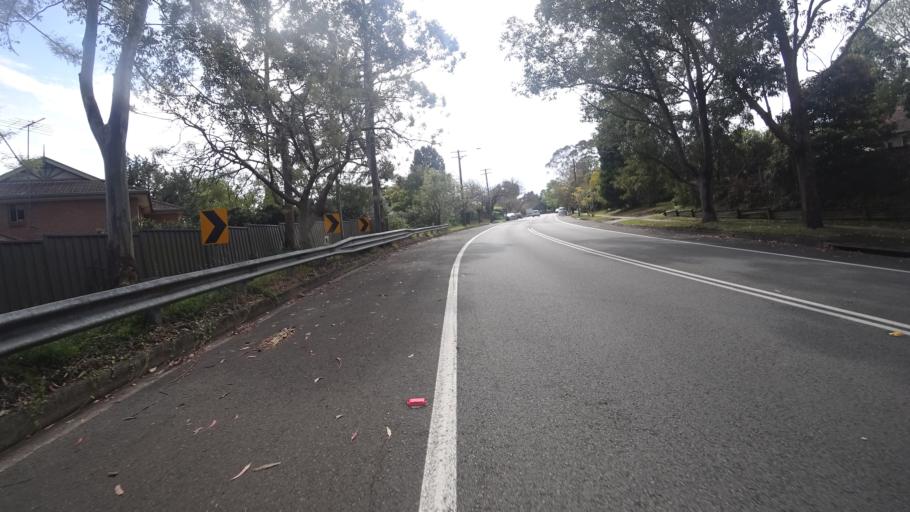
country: AU
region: New South Wales
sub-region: City of Sydney
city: North Turramurra
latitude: -33.7223
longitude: 151.1404
